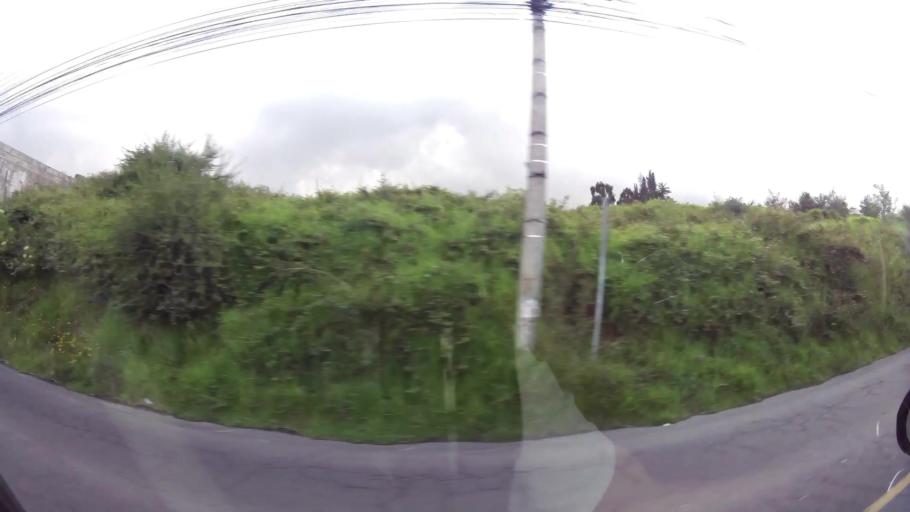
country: EC
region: Pichincha
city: Sangolqui
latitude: -0.2884
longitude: -78.4891
